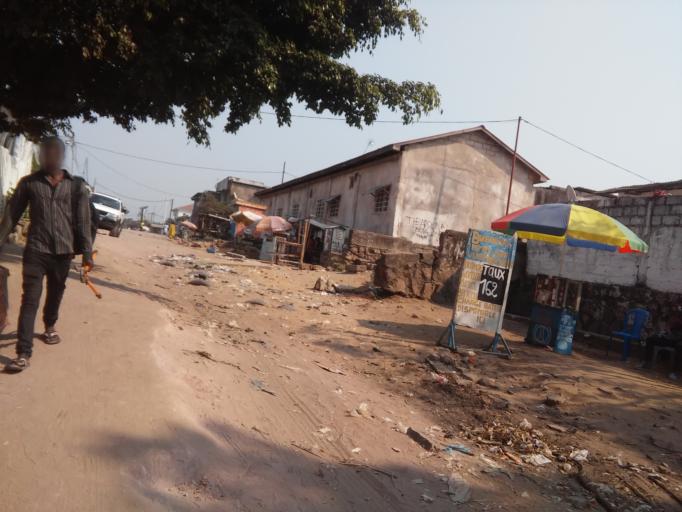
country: CD
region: Kinshasa
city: Kinshasa
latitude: -4.3442
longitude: 15.2646
